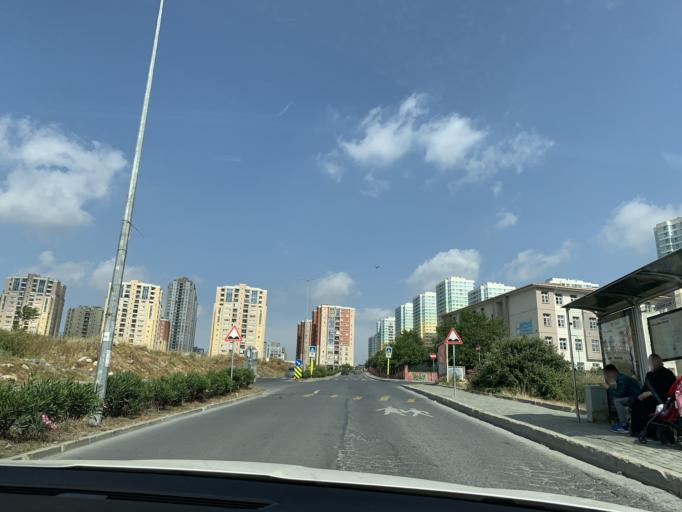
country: TR
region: Istanbul
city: Esenyurt
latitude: 41.0654
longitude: 28.7065
